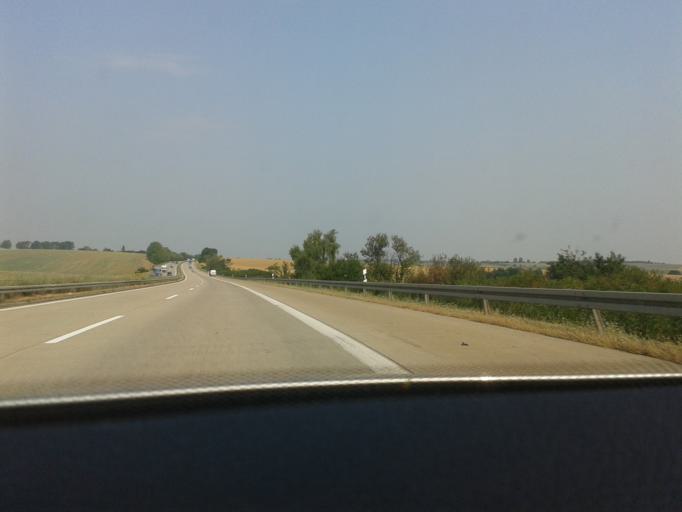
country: DE
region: Saxony
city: Mochau
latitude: 51.1317
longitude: 13.1634
